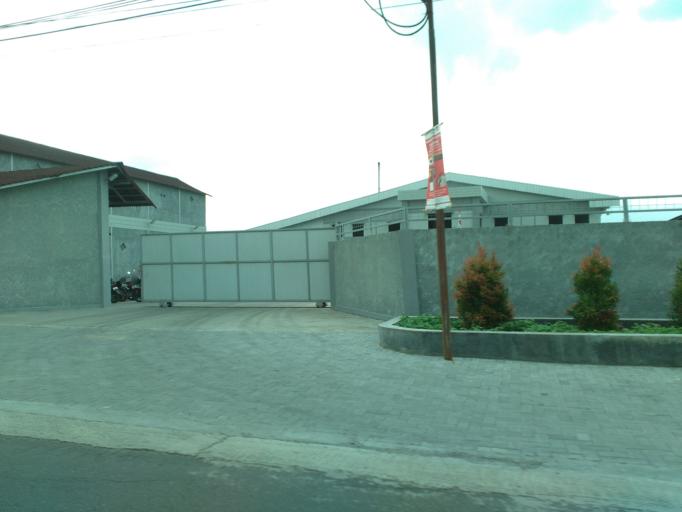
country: ID
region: Central Java
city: Ceper
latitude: -7.6636
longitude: 110.6641
